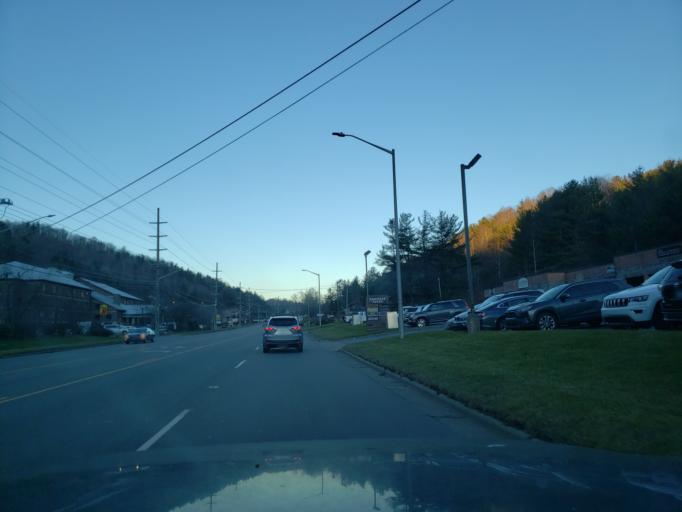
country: US
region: North Carolina
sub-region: Watauga County
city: Boone
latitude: 36.2046
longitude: -81.6924
